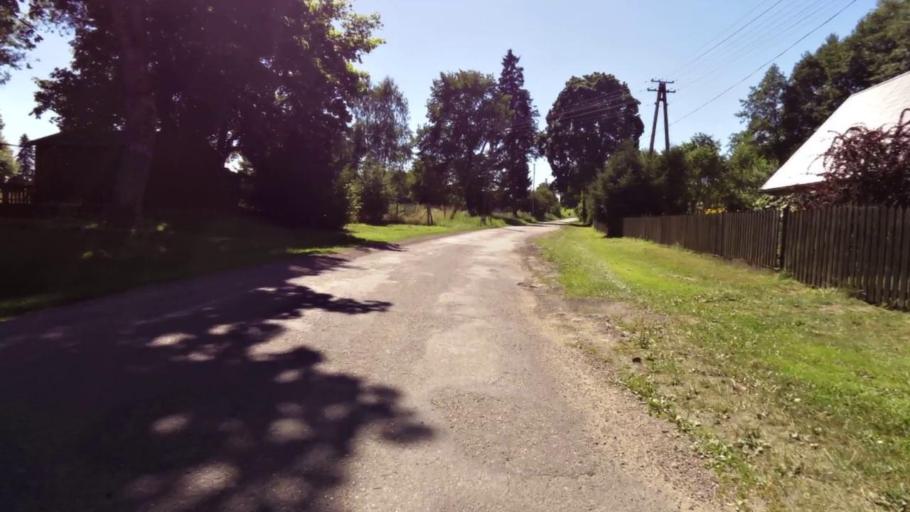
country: PL
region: West Pomeranian Voivodeship
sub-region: Powiat szczecinecki
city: Bialy Bor
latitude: 53.8732
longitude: 16.7972
